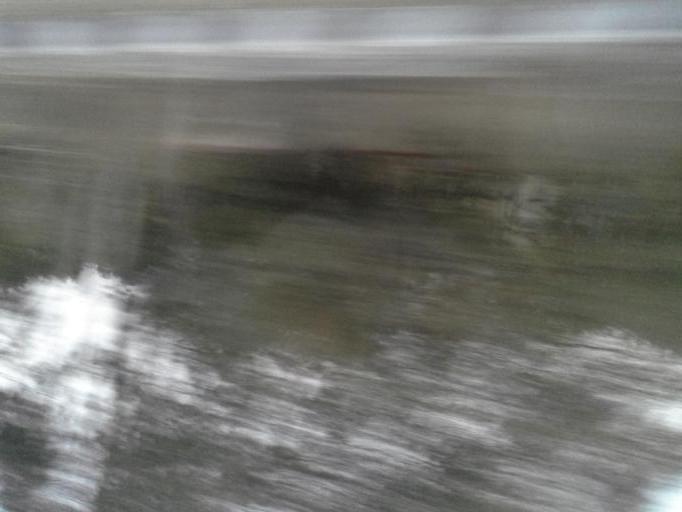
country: IN
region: Telangana
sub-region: Hyderabad
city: Hyderabad
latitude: 17.3223
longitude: 78.3741
